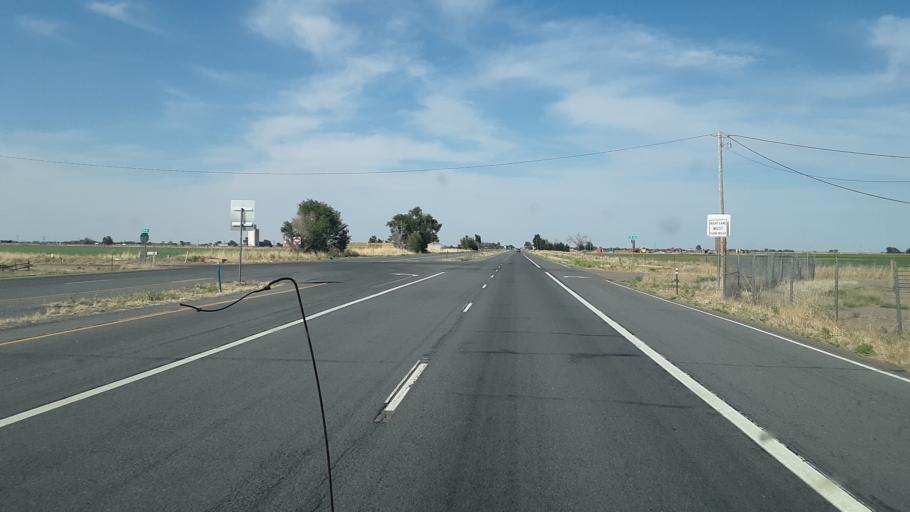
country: US
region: Colorado
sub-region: Bent County
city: Las Animas
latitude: 38.0934
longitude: -103.1618
